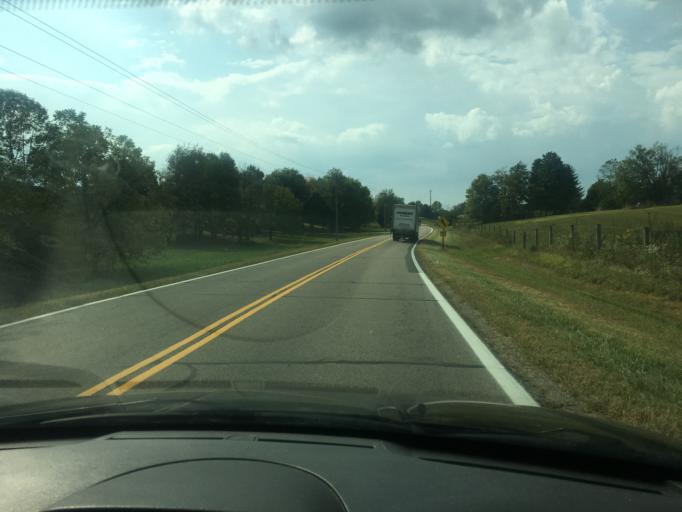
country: US
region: Ohio
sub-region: Champaign County
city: Urbana
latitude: 40.1567
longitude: -83.8219
